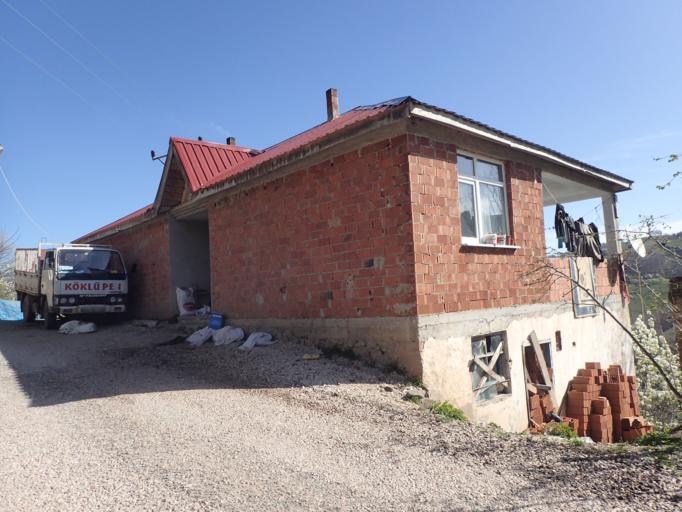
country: TR
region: Ordu
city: Aybasti
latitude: 40.6990
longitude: 37.2752
